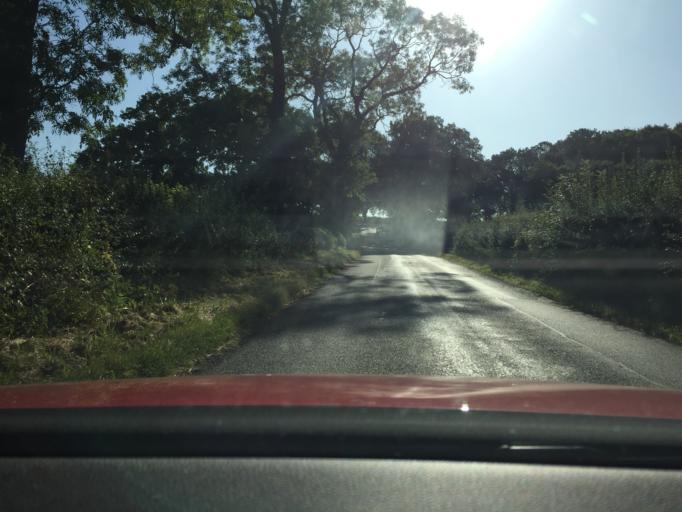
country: GB
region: England
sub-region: Leicestershire
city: Houghton on the Hill
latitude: 52.6362
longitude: -0.9541
